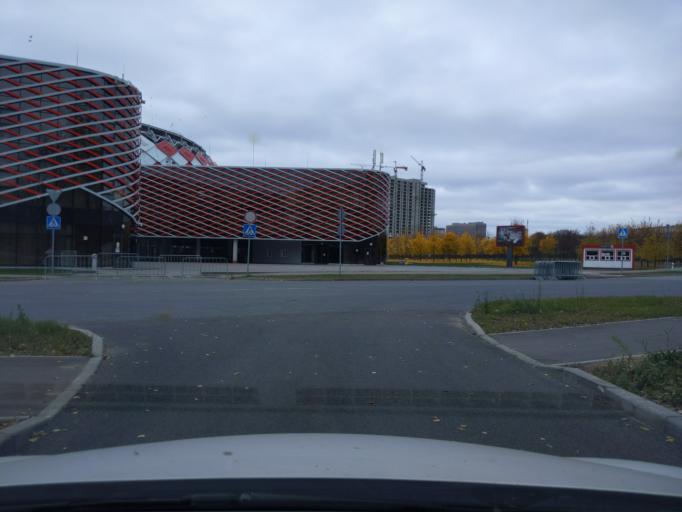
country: RU
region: Moscow
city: Pokrovskoye-Streshnevo
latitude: 55.8178
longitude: 37.4439
